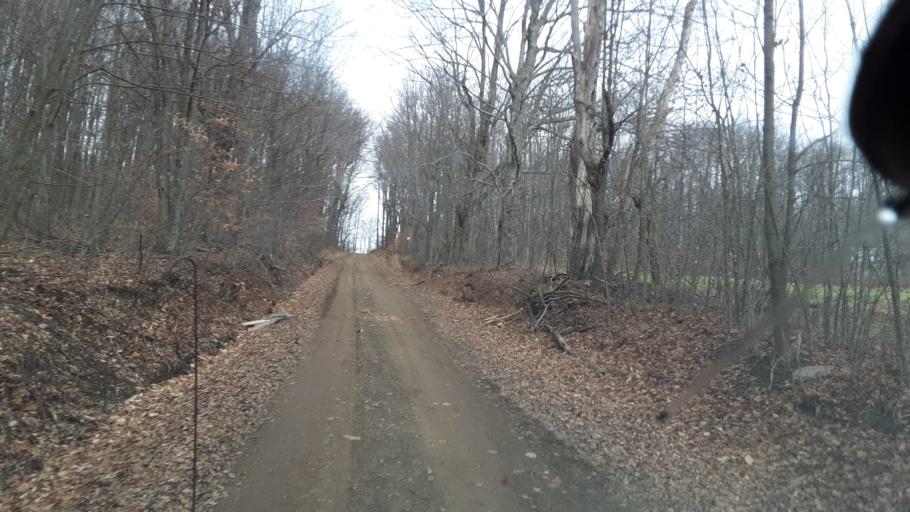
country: US
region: Pennsylvania
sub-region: Tioga County
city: Westfield
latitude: 41.9193
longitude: -77.7044
